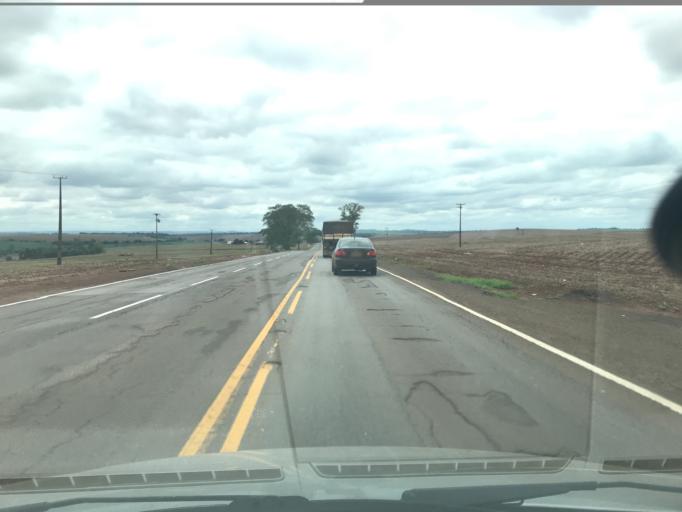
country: BR
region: Parana
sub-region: Terra Boa
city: Terra Boa
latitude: -23.6040
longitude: -52.4102
